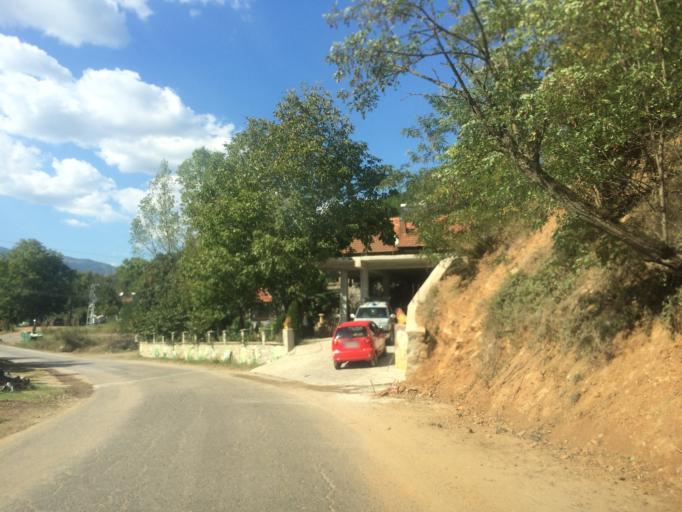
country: MK
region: Makedonska Kamenica
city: Makedonska Kamenica
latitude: 42.0371
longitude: 22.5822
